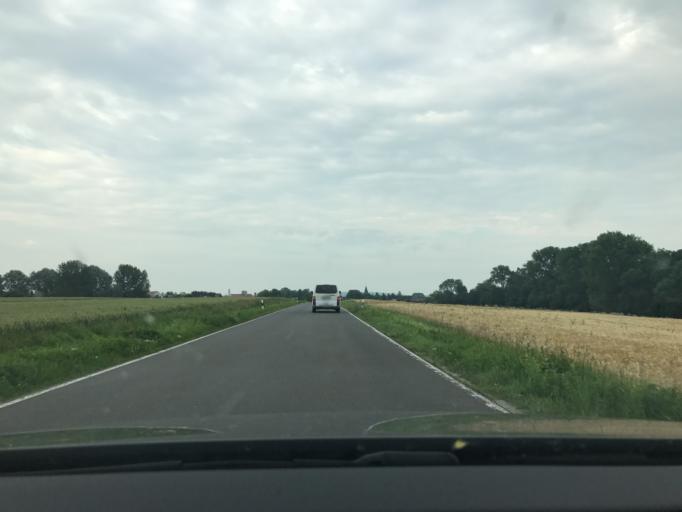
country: DE
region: Thuringia
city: Anrode
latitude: 51.2551
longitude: 10.3785
